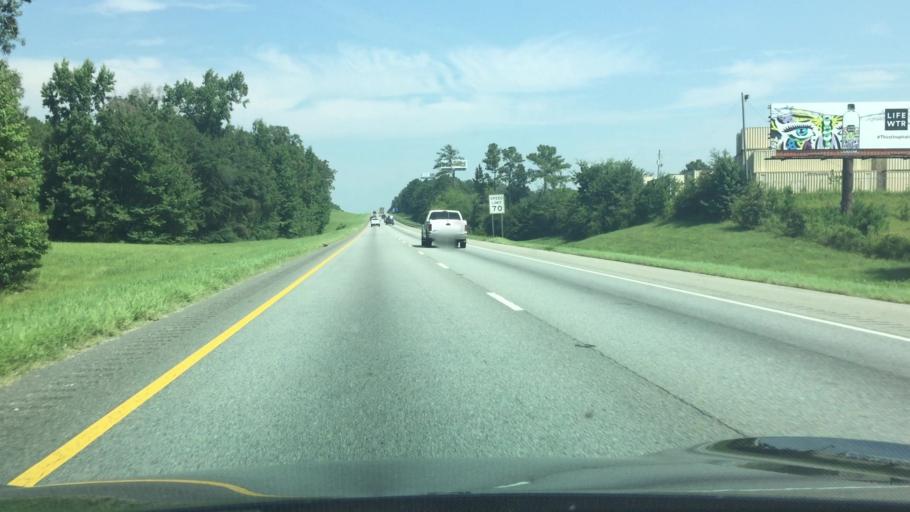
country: US
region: Alabama
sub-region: Shelby County
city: Alabaster
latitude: 33.1848
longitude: -86.7823
